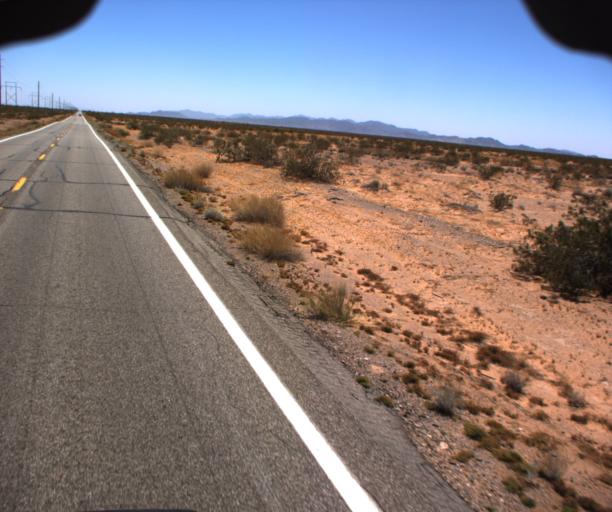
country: US
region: Arizona
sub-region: La Paz County
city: Quartzsite
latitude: 33.8789
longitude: -114.2170
